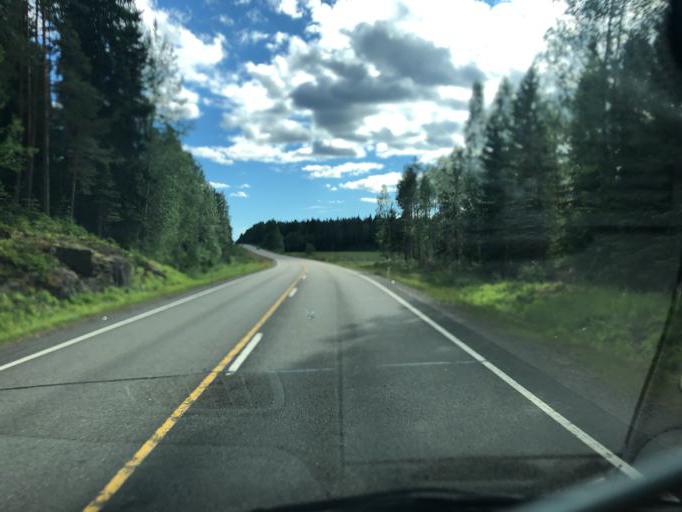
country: FI
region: Kymenlaakso
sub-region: Kouvola
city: Kouvola
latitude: 60.9970
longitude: 26.9267
